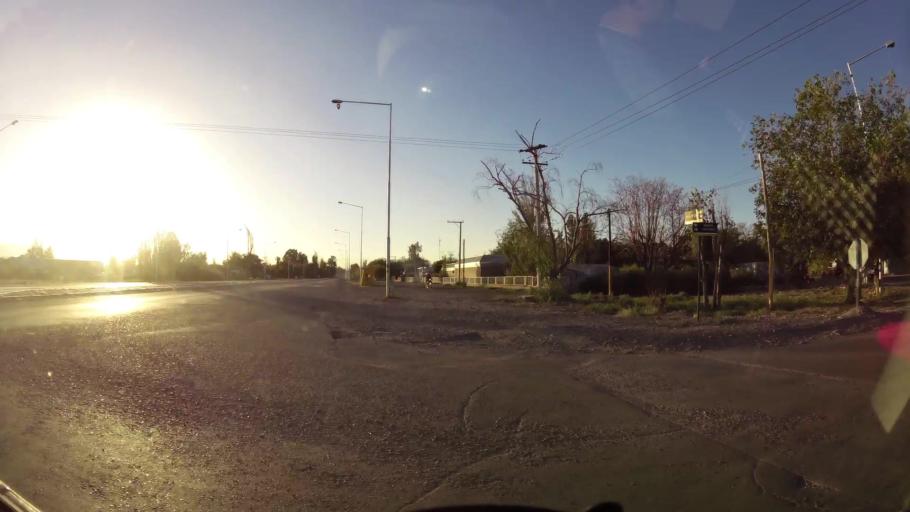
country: AR
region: San Juan
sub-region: Departamento de Santa Lucia
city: Santa Lucia
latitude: -31.5533
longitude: -68.4759
